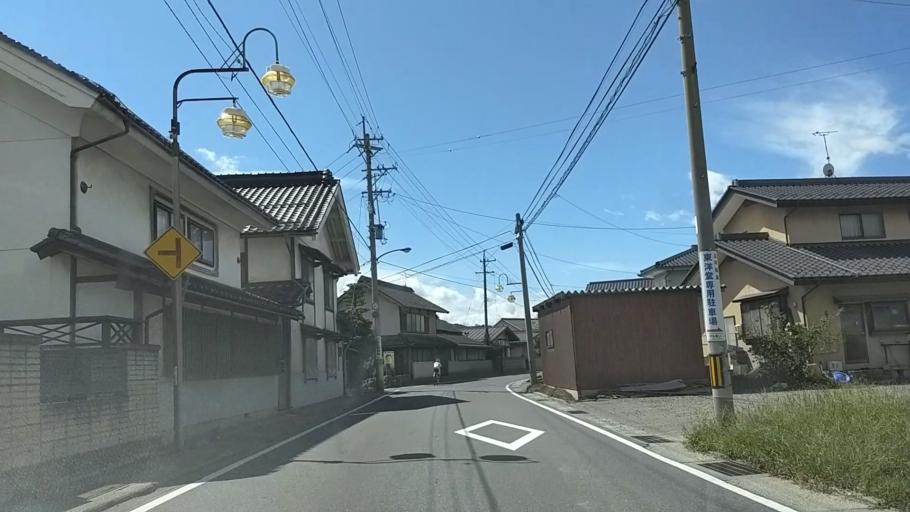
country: JP
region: Nagano
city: Suzaka
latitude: 36.6205
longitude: 138.2554
